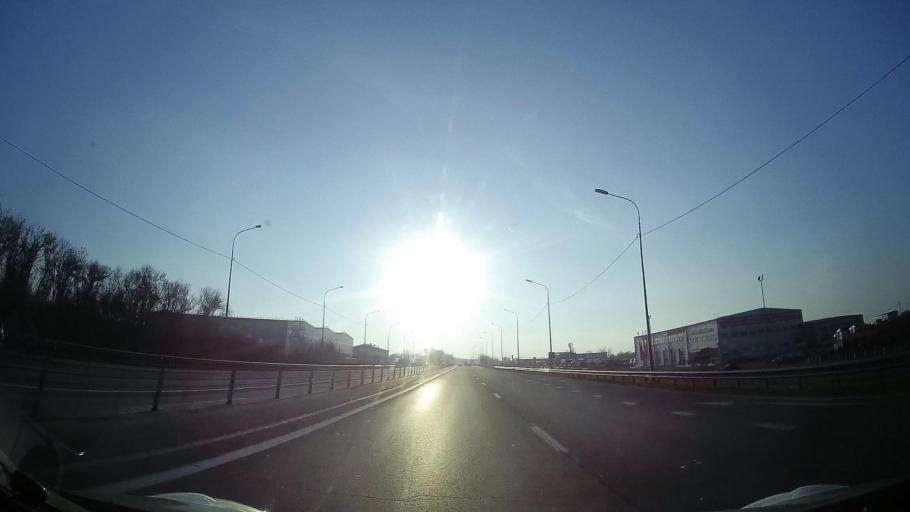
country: RU
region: Rostov
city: Ol'ginskaya
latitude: 47.1215
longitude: 39.8647
